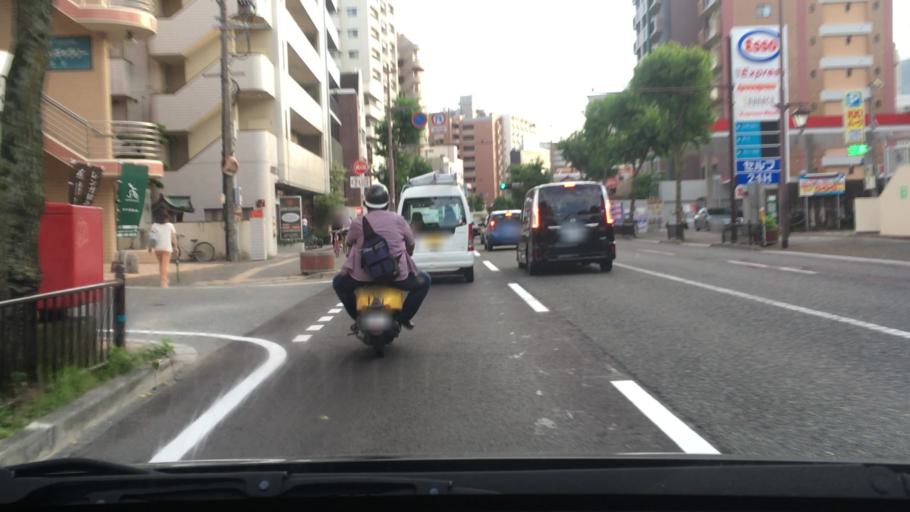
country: JP
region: Fukuoka
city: Fukuoka-shi
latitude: 33.5802
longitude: 130.3816
